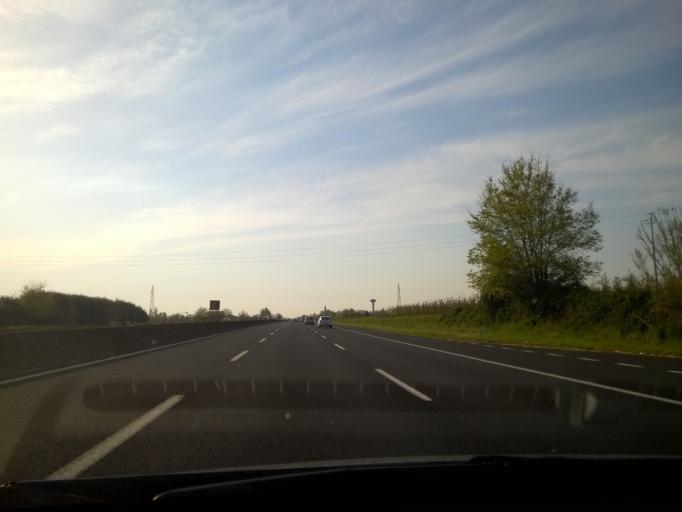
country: IT
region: Emilia-Romagna
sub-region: Forli-Cesena
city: Forli
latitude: 44.2636
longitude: 12.0575
